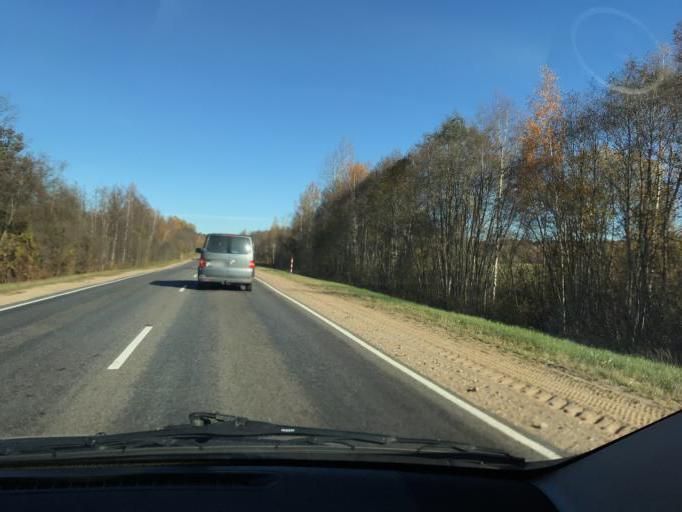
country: BY
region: Vitebsk
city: Polatsk
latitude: 55.3295
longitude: 28.7860
